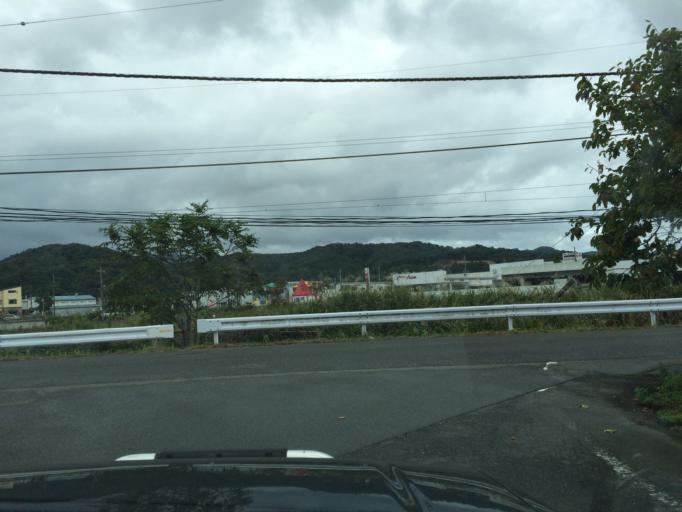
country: JP
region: Hyogo
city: Toyooka
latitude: 35.4802
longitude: 134.7855
